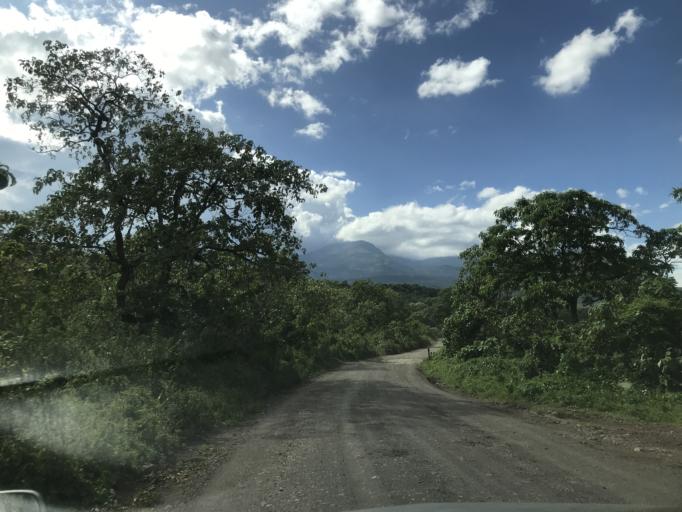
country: TZ
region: Arusha
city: Usa River
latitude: -3.3052
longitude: 36.8758
